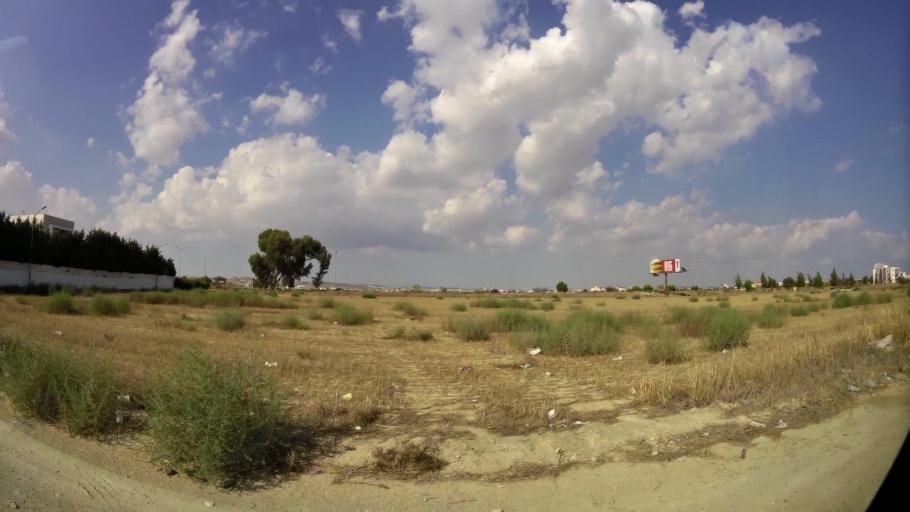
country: CY
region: Larnaka
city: Dhromolaxia
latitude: 34.9072
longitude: 33.5792
